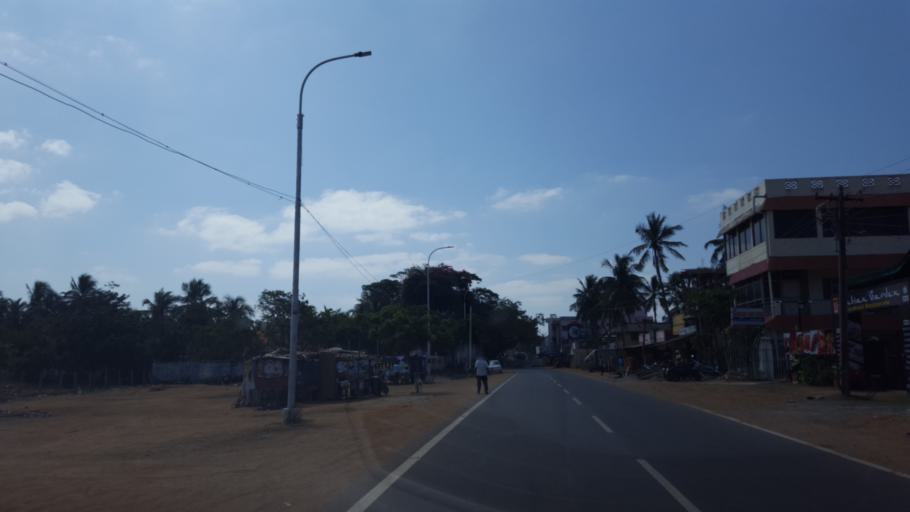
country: IN
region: Tamil Nadu
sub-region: Kancheepuram
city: Mamallapuram
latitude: 12.6257
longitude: 80.1943
